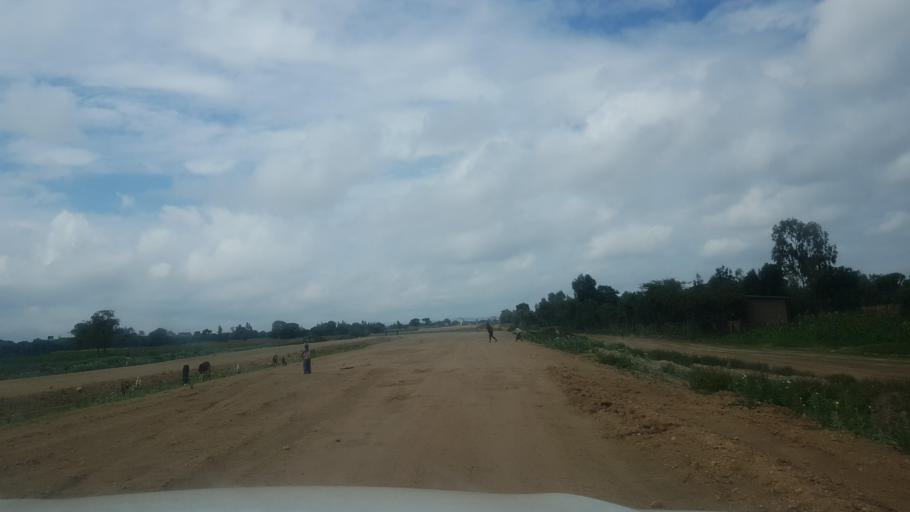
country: ET
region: Oromiya
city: Shashemene
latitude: 7.2647
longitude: 38.5968
